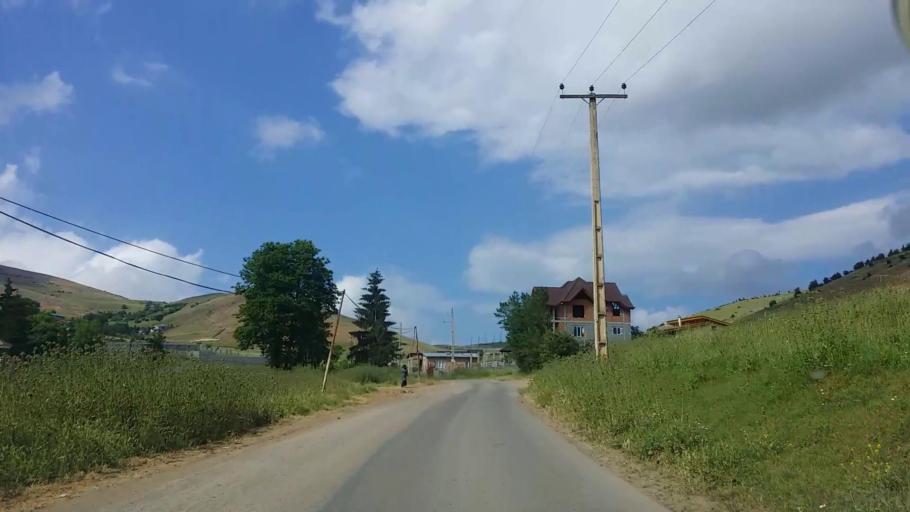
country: IR
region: Mazandaran
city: Chalus
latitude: 36.5211
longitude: 51.2607
